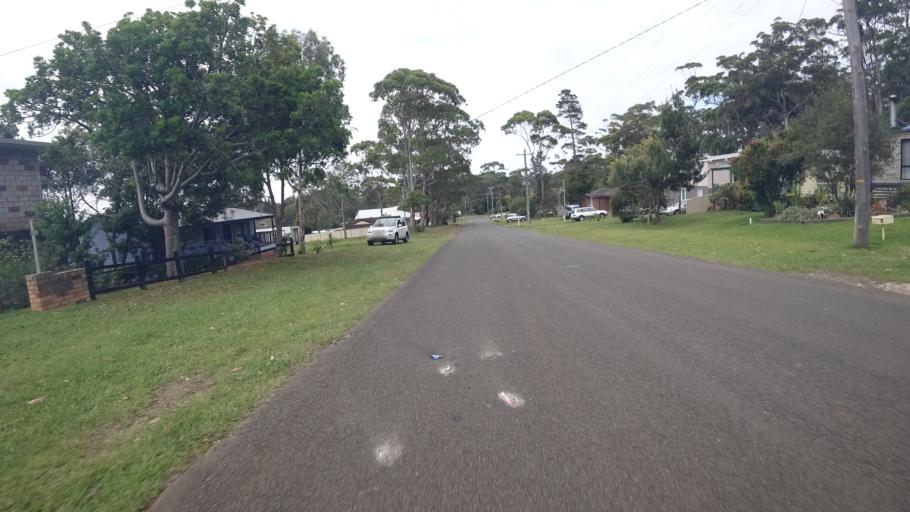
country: AU
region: New South Wales
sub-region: Shoalhaven Shire
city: Milton
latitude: -35.2567
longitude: 150.5133
